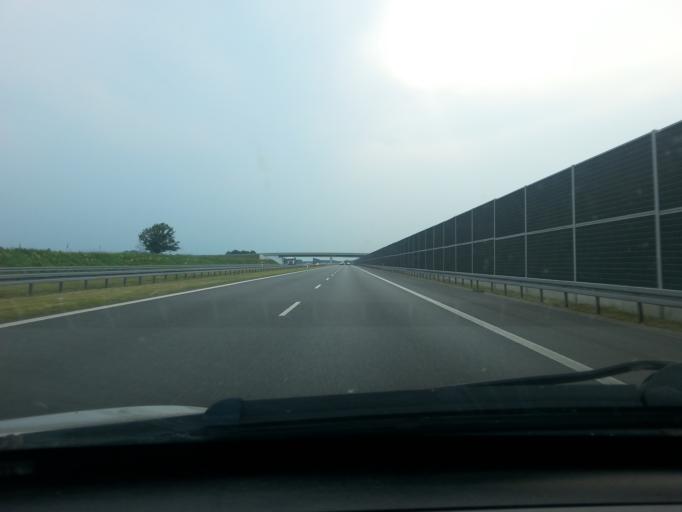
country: PL
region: Masovian Voivodeship
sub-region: Powiat zyrardowski
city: Guzow
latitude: 52.0742
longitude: 20.2637
